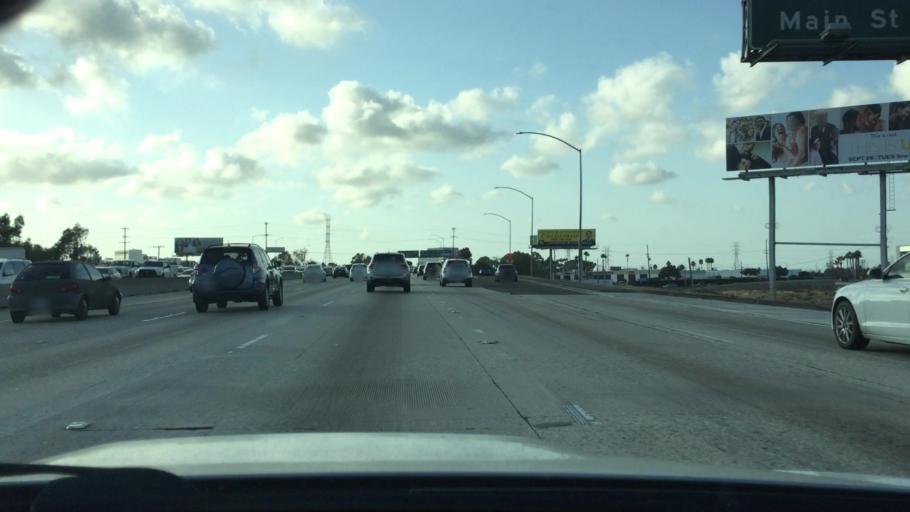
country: US
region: California
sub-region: Los Angeles County
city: Carson
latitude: 33.8513
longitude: -118.2774
